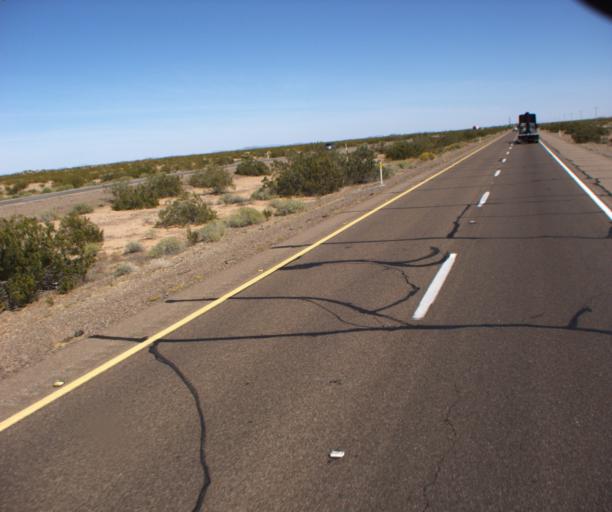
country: US
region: Arizona
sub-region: Yuma County
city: Wellton
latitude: 32.7788
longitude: -113.5877
